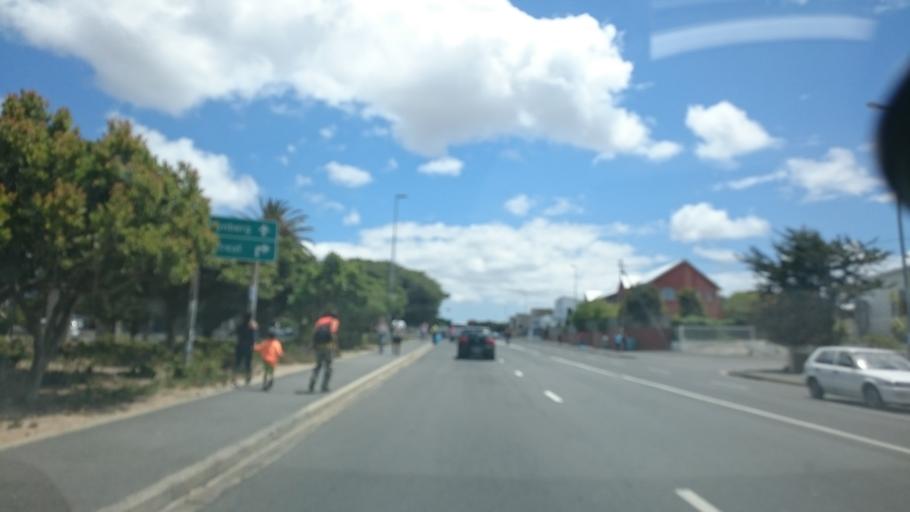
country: ZA
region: Western Cape
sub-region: City of Cape Town
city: Bergvliet
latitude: -34.0638
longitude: 18.4593
